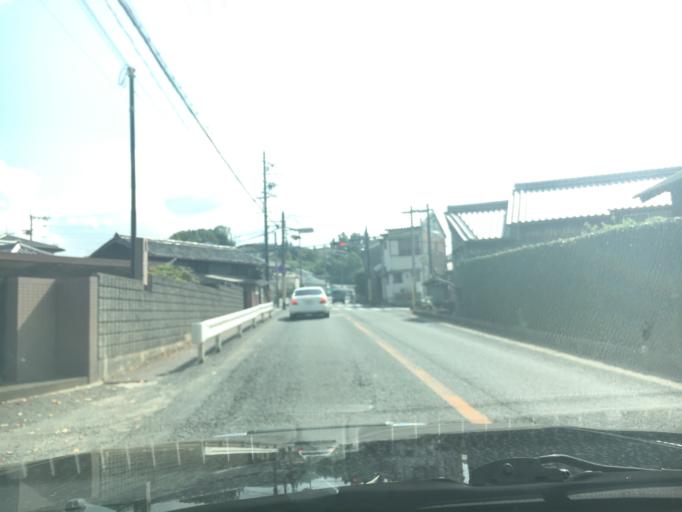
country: JP
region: Nara
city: Nara-shi
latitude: 34.7052
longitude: 135.8345
